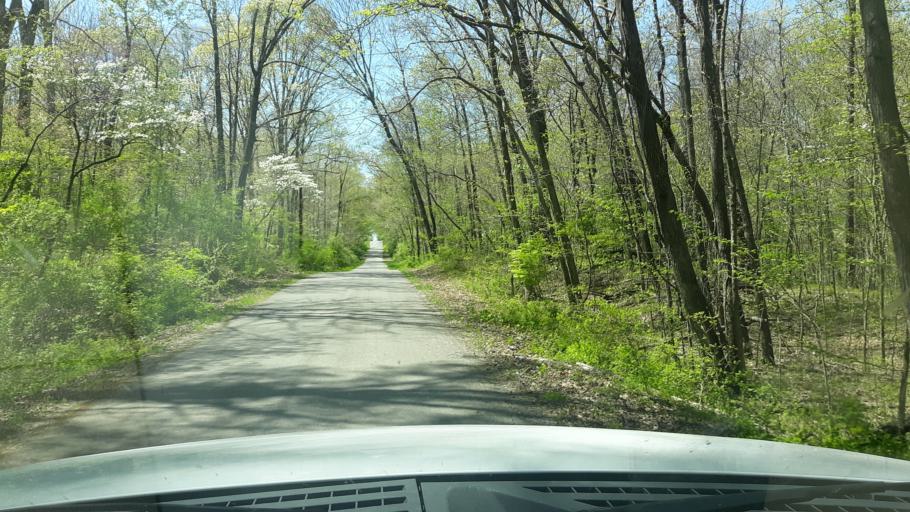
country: US
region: Illinois
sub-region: Saline County
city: Harrisburg
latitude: 37.8596
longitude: -88.6275
